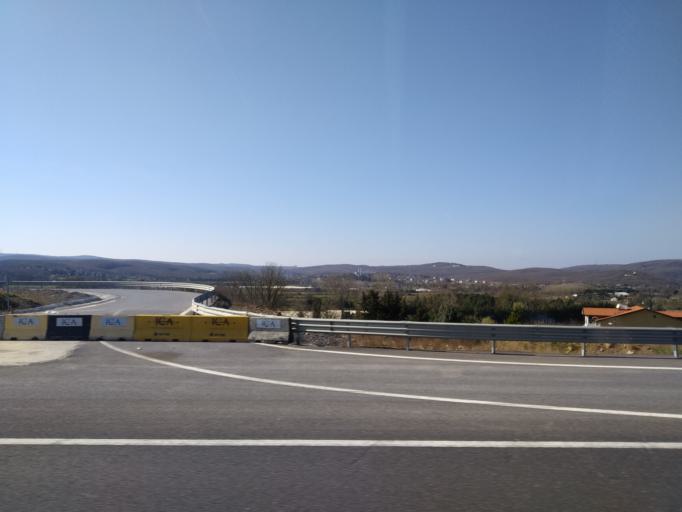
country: TR
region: Istanbul
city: Mahmut Sevket Pasa
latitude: 41.1282
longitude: 29.2860
